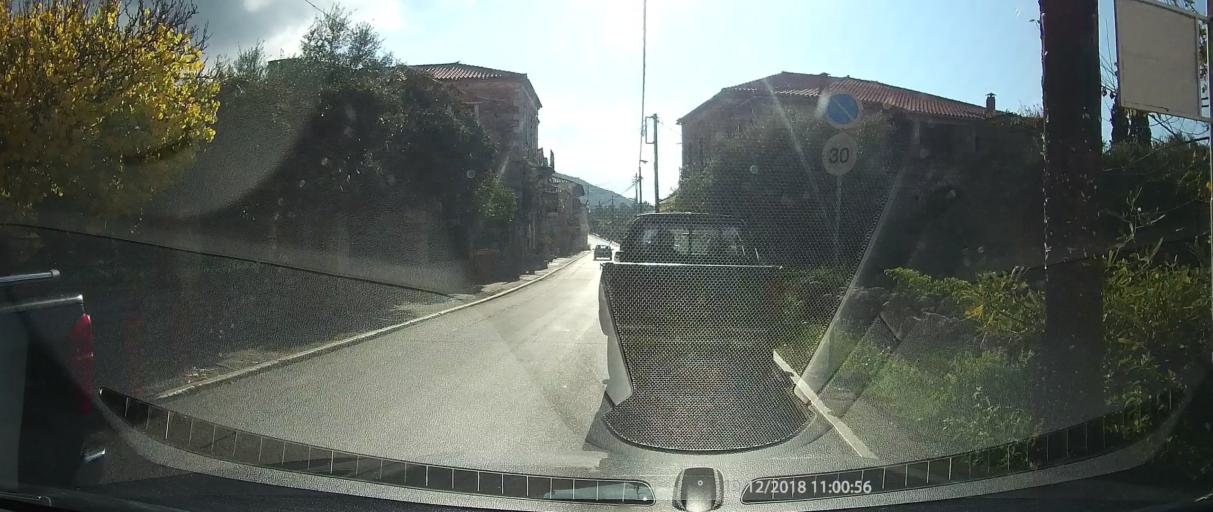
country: GR
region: Peloponnese
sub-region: Nomos Messinias
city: Kardamyli
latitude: 36.8870
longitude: 22.2329
